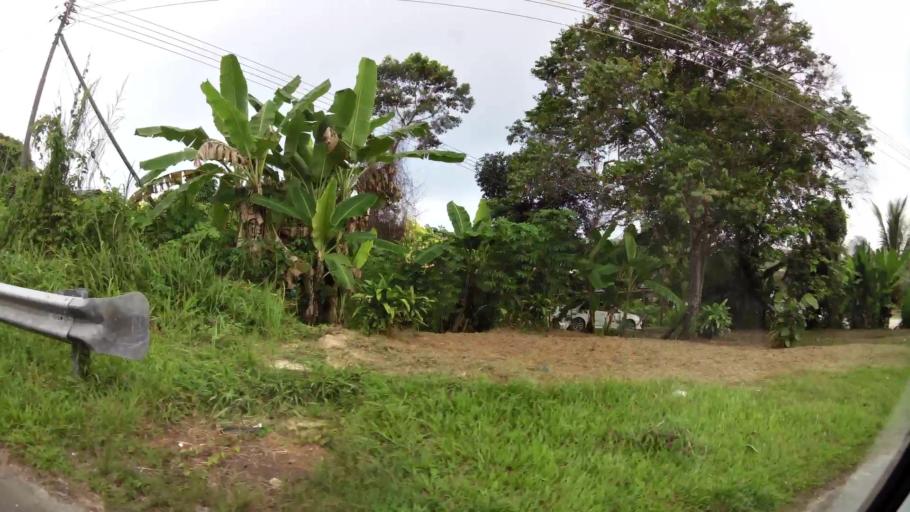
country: BN
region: Brunei and Muara
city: Bandar Seri Begawan
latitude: 4.9045
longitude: 114.9931
